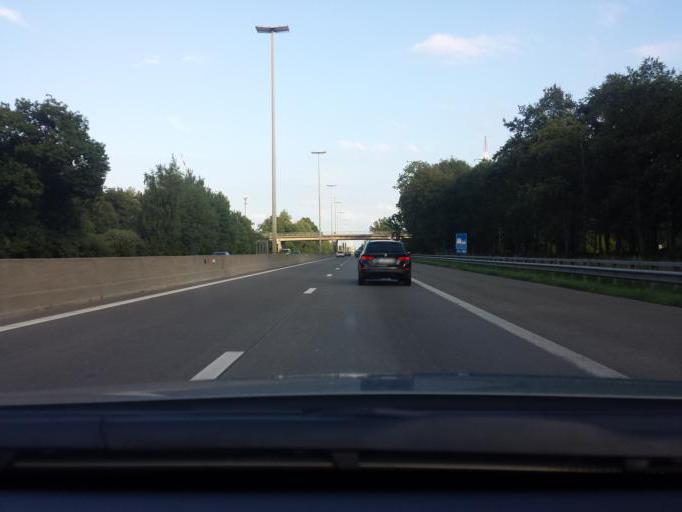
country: BE
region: Flanders
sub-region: Provincie Limburg
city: Tessenderlo
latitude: 51.0639
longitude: 5.1559
